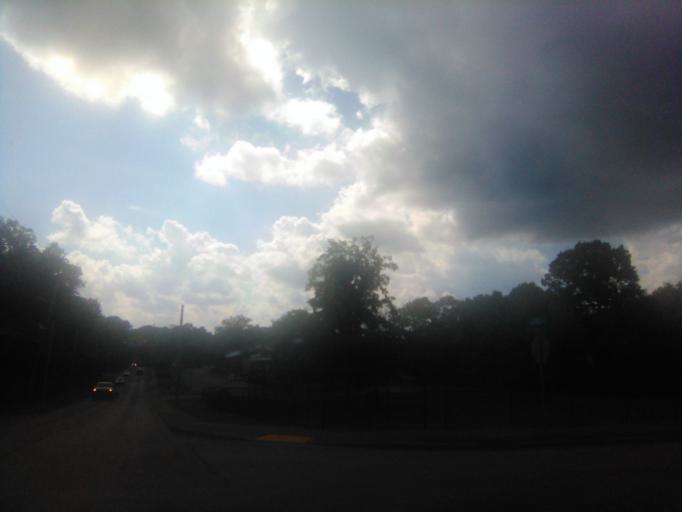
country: US
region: Tennessee
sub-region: Davidson County
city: Belle Meade
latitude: 36.1021
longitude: -86.8306
